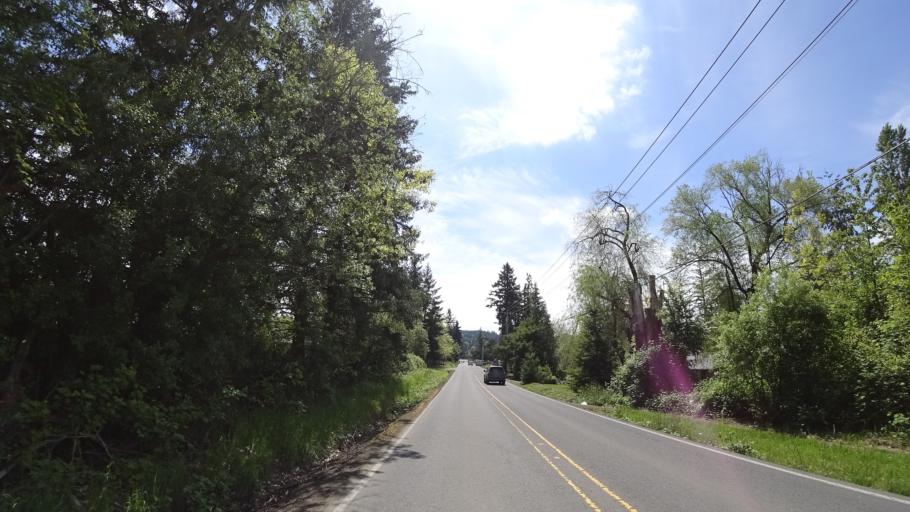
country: US
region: Oregon
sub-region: Washington County
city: Aloha
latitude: 45.4755
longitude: -122.8817
